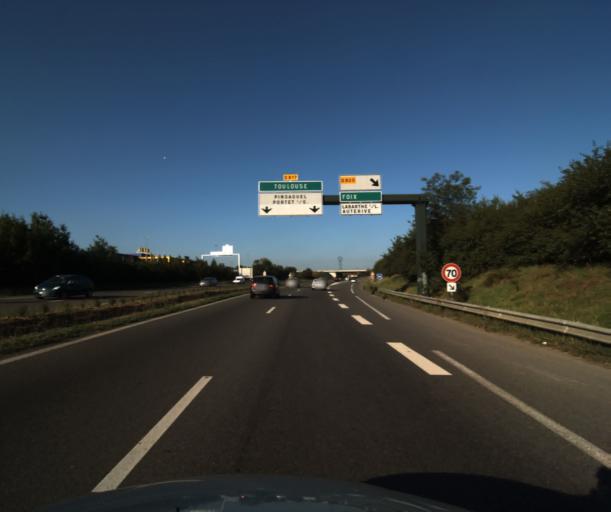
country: FR
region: Midi-Pyrenees
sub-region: Departement de la Haute-Garonne
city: Pinsaguel
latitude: 43.5152
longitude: 1.3756
